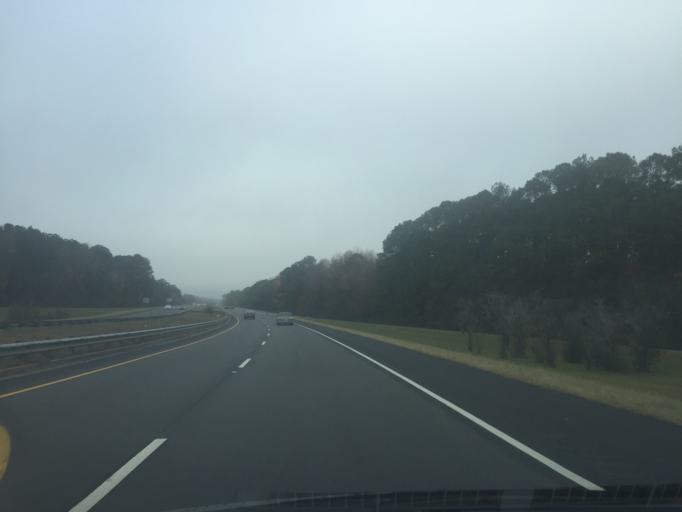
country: US
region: Georgia
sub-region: Chatham County
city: Georgetown
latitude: 32.0010
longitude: -81.2512
